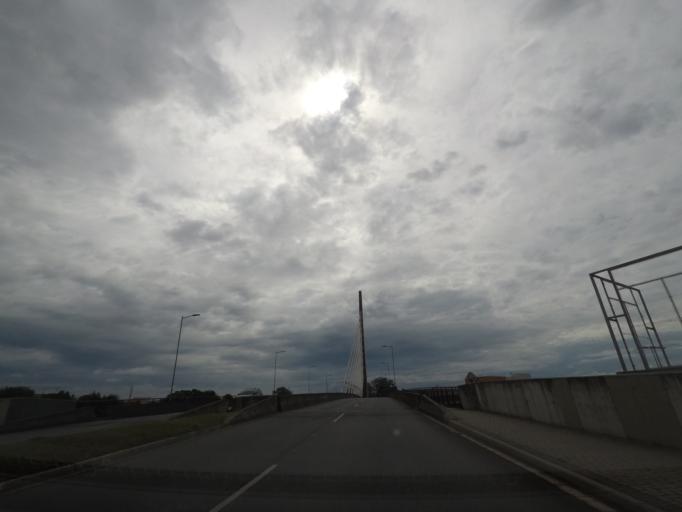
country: BR
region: Parana
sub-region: Pinhais
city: Pinhais
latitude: -25.4655
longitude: -49.2353
